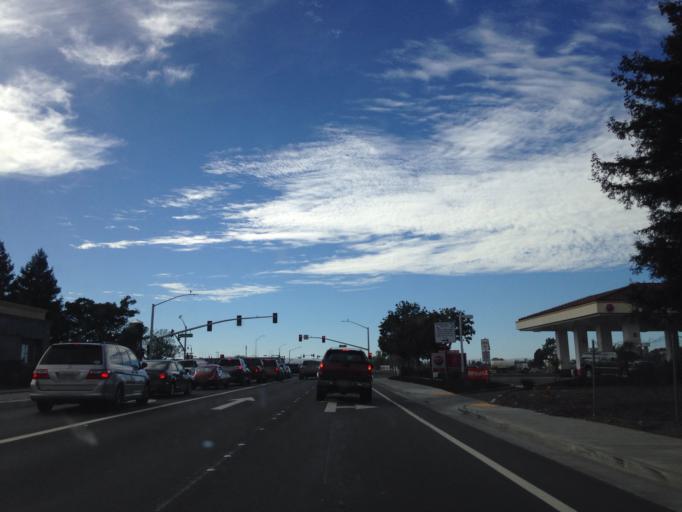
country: US
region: California
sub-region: Sonoma County
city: Rohnert Park
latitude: 38.3634
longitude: -122.7138
